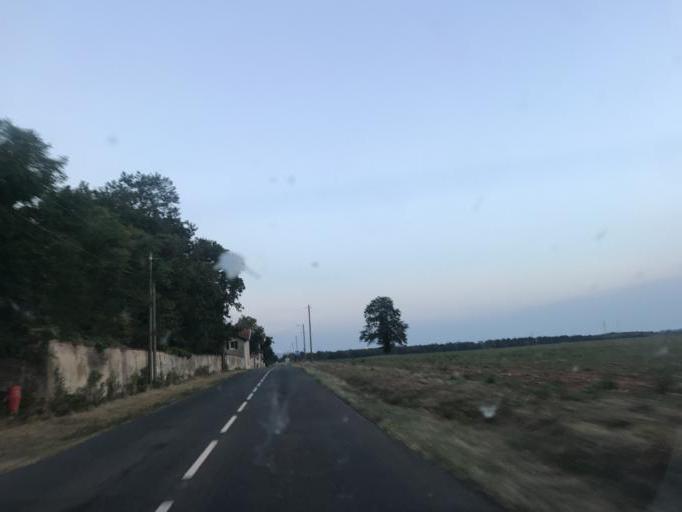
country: FR
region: Rhone-Alpes
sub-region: Departement de l'Ain
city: Chazey-sur-Ain
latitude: 45.8663
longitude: 5.2798
